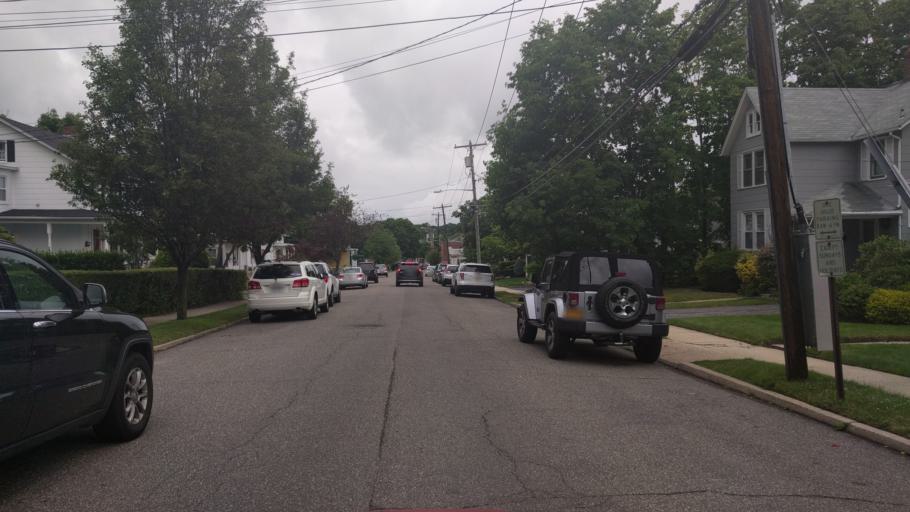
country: US
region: New York
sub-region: Suffolk County
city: Huntington
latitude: 40.8680
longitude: -73.4280
